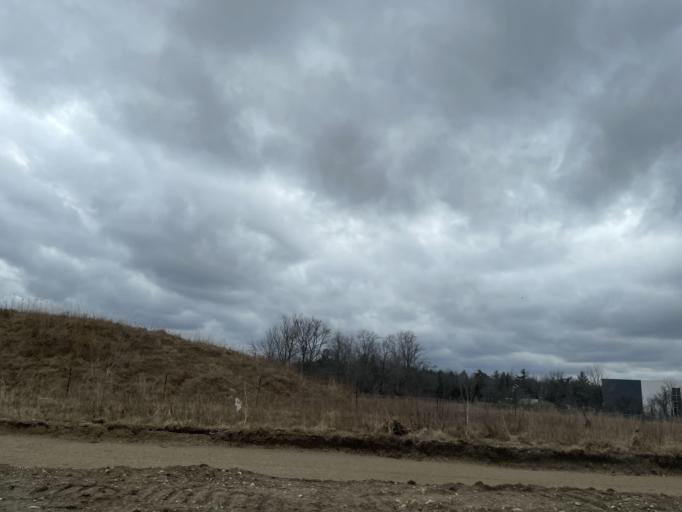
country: CA
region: Ontario
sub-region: Wellington County
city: Guelph
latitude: 43.4928
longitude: -80.2199
